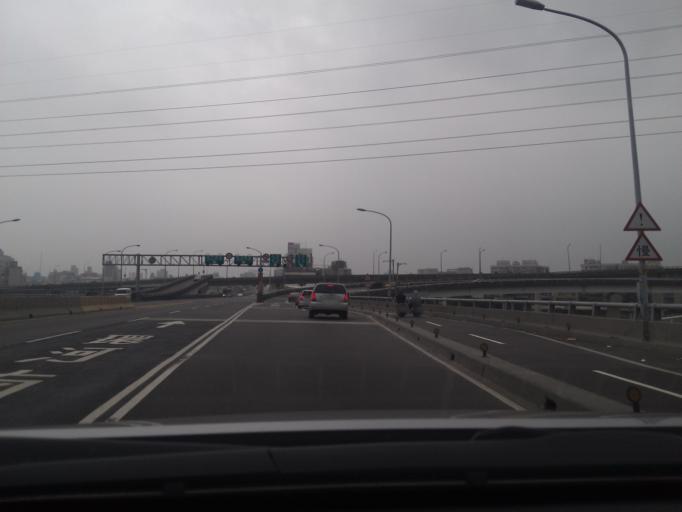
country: TW
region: Taipei
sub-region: Taipei
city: Banqiao
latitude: 25.0355
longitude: 121.4878
